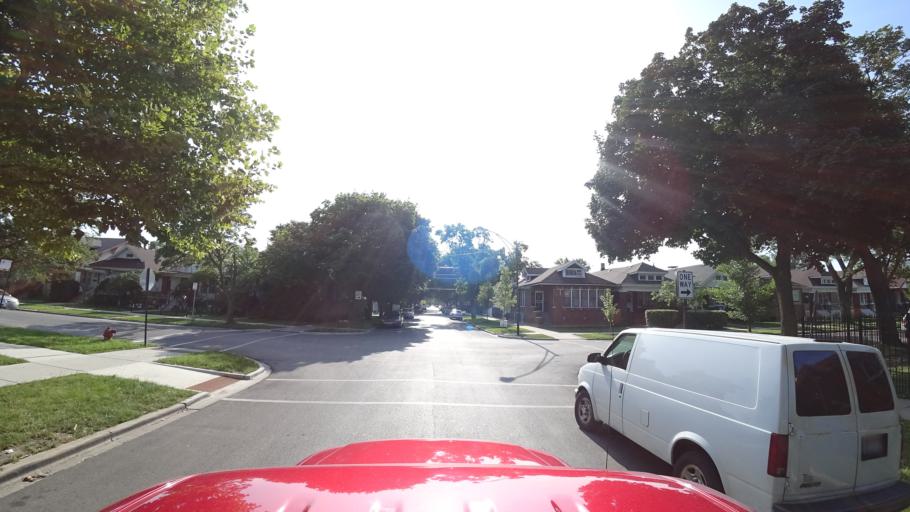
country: US
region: Illinois
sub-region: Cook County
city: Hometown
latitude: 41.7880
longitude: -87.7061
